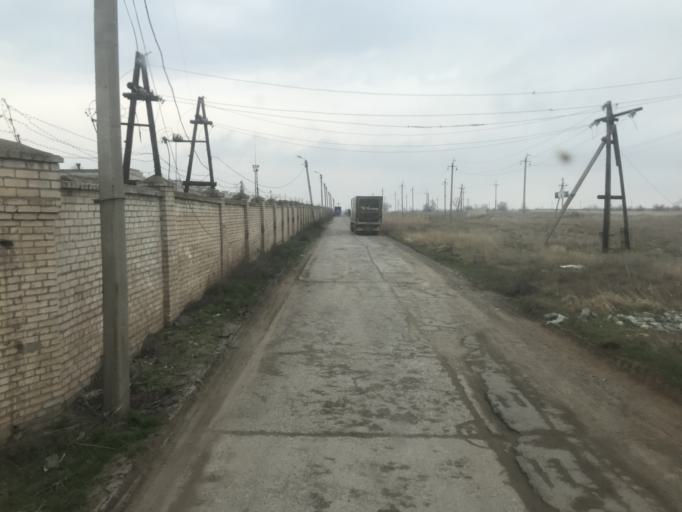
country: RU
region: Volgograd
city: Krasnoslobodsk
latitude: 48.5332
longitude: 44.5854
